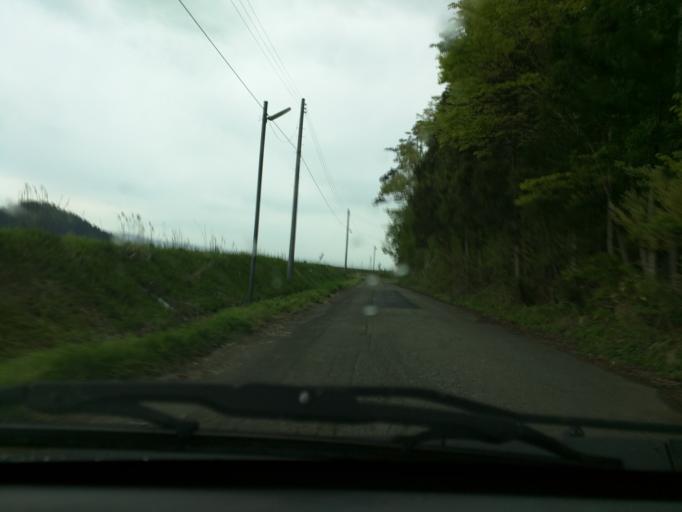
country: JP
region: Fukushima
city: Kitakata
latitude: 37.4291
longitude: 139.8884
